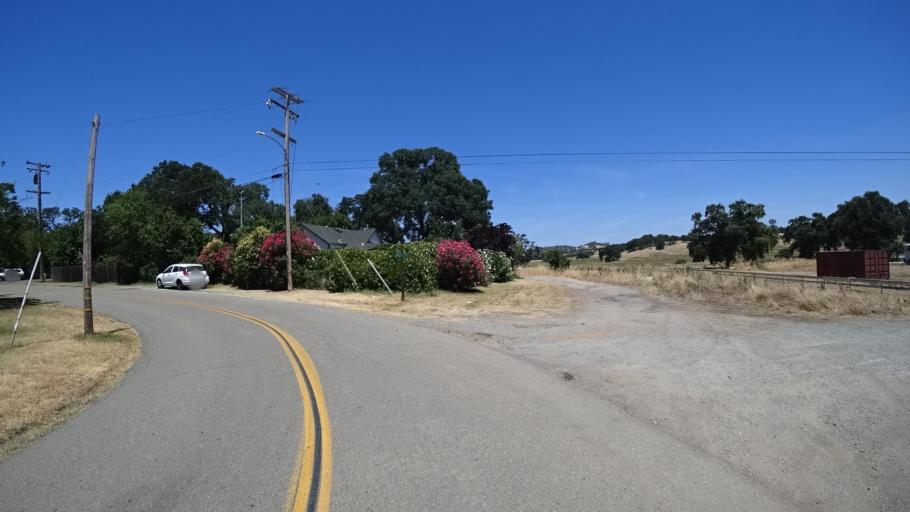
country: US
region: California
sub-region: Calaveras County
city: Valley Springs
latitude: 38.1941
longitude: -120.8269
